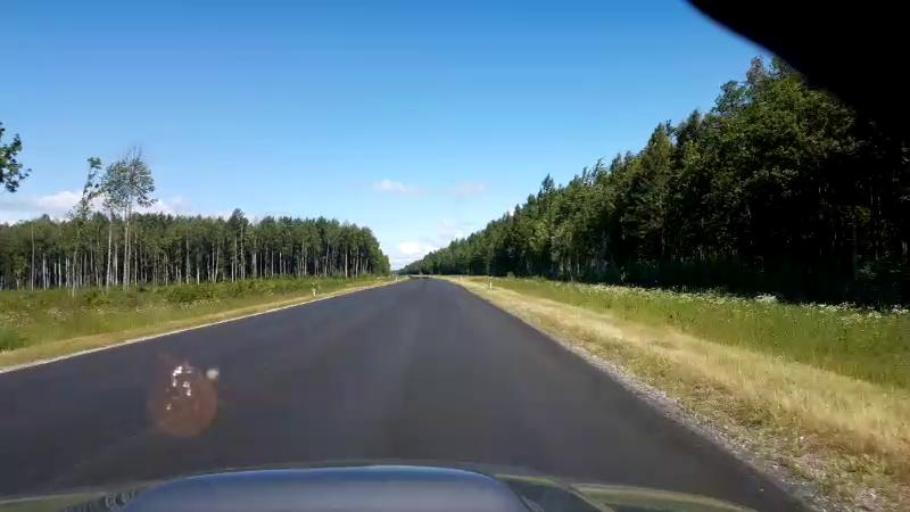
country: LV
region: Salacgrivas
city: Ainazi
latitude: 57.9137
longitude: 24.4199
